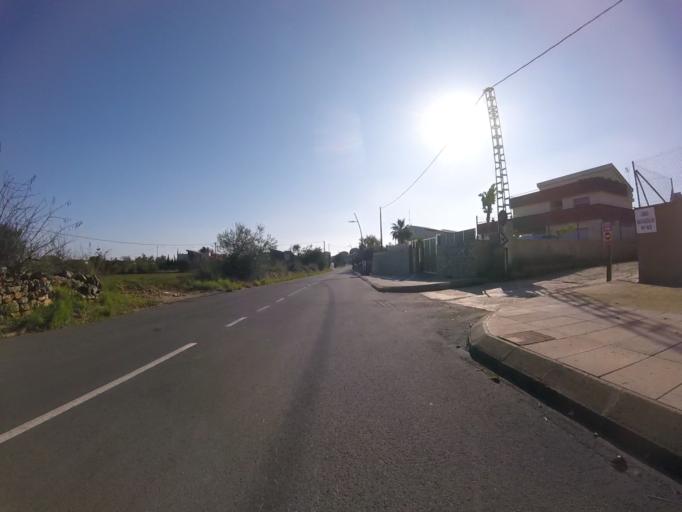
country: ES
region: Valencia
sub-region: Provincia de Castello
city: Peniscola
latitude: 40.3847
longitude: 0.3799
